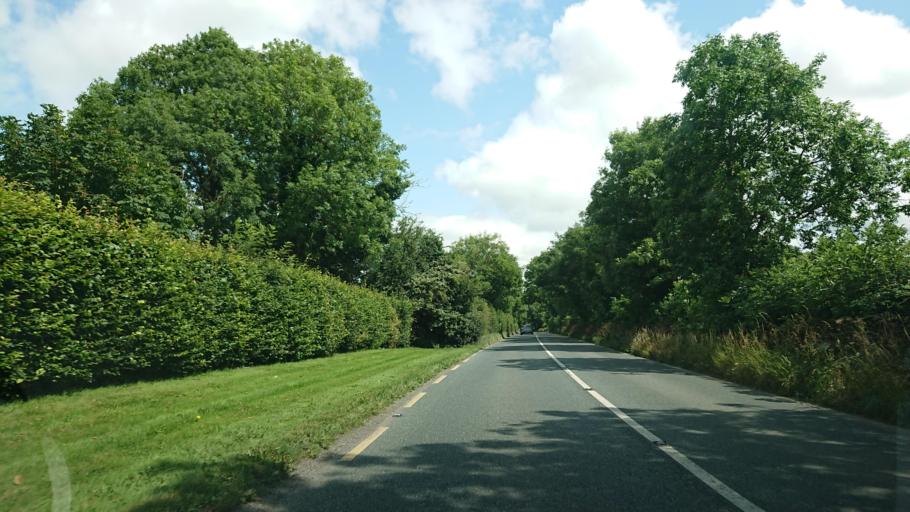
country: IE
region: Leinster
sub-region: Kildare
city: Kilcock
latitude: 53.3906
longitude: -6.6941
